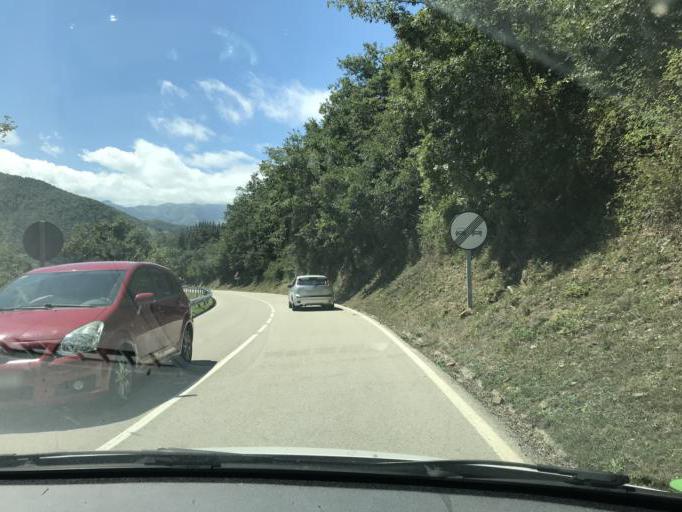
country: ES
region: Cantabria
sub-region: Provincia de Cantabria
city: Cabezon de Liebana
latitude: 43.0767
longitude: -4.4827
